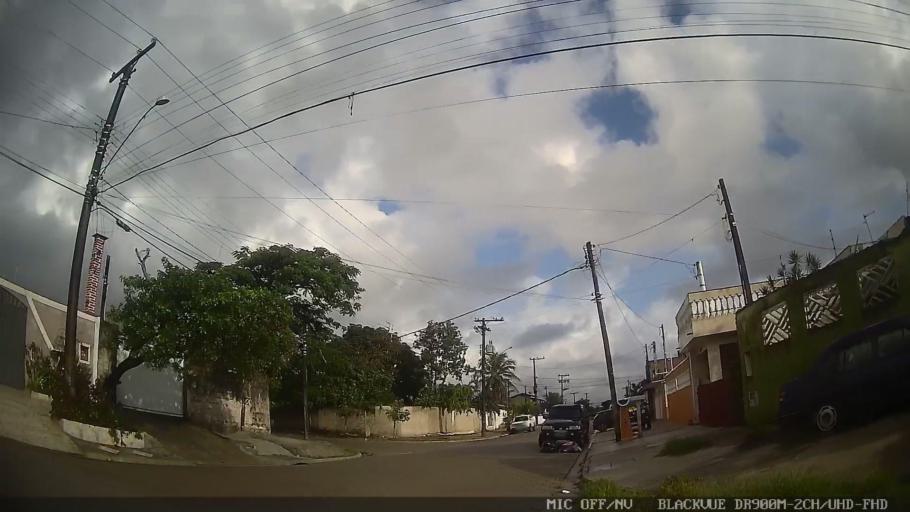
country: BR
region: Sao Paulo
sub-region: Itanhaem
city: Itanhaem
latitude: -24.1829
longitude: -46.8565
